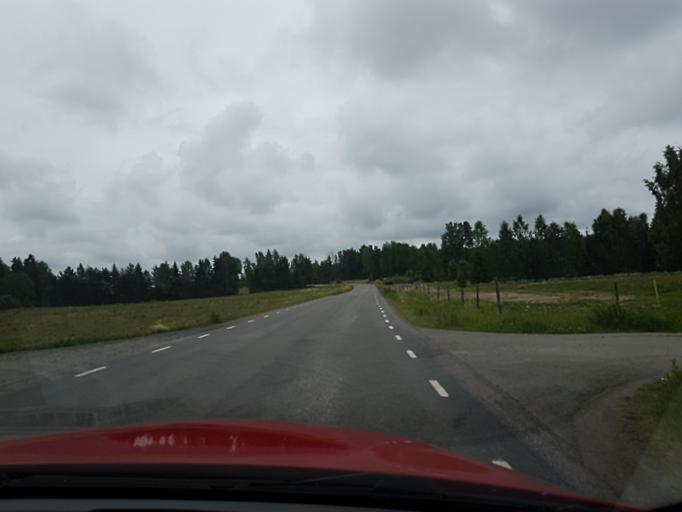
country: SE
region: Vaestra Goetaland
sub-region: Tidaholms Kommun
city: Olofstorp
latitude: 58.3491
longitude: 13.9623
